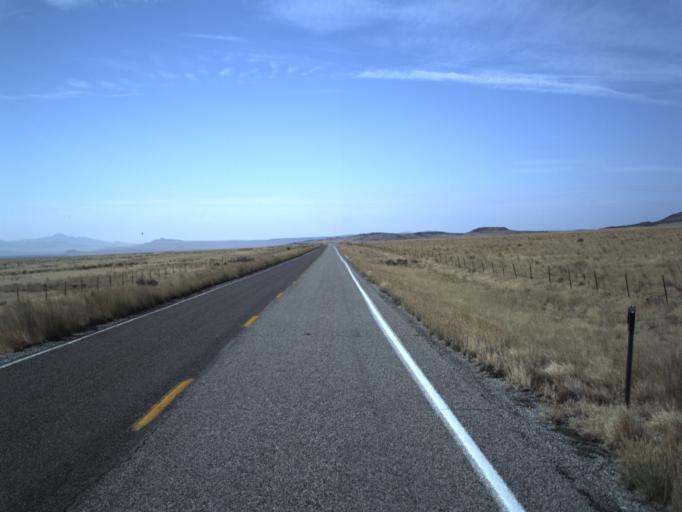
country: US
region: Idaho
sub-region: Oneida County
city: Malad City
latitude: 41.8761
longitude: -113.1201
